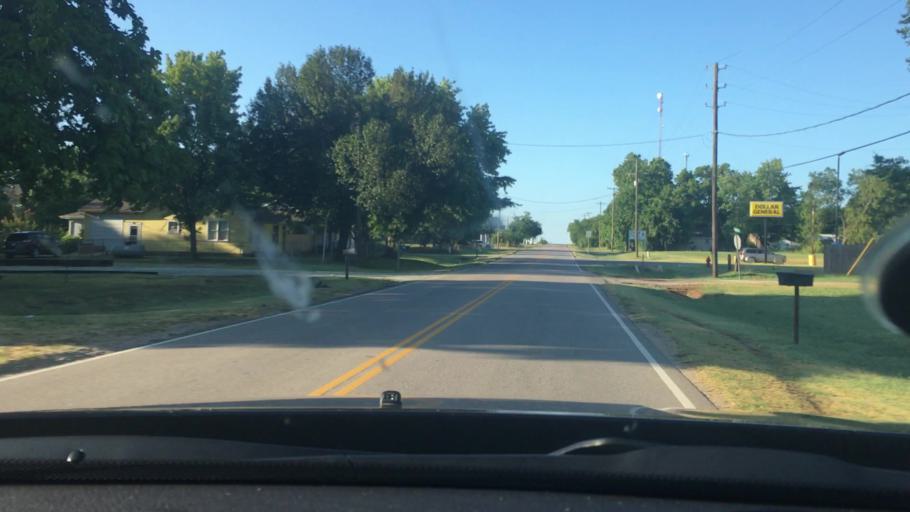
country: US
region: Oklahoma
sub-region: Murray County
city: Sulphur
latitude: 34.6246
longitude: -96.8447
